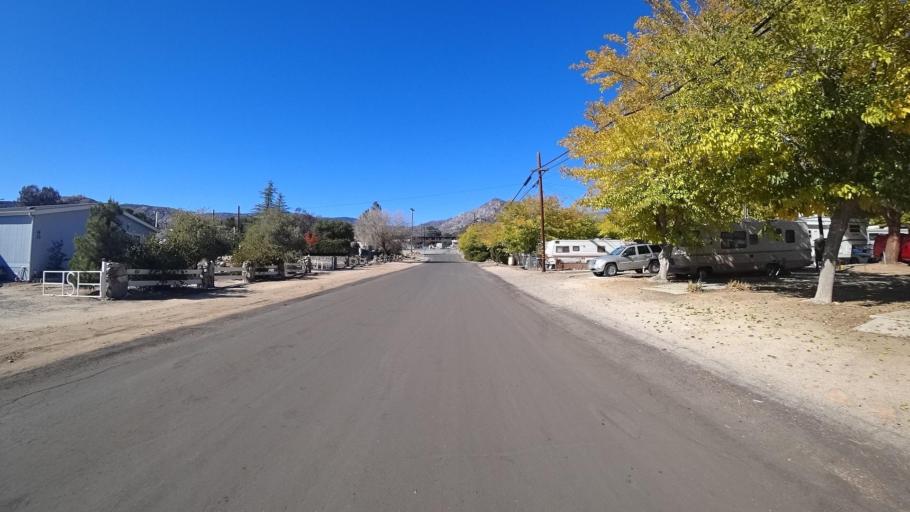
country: US
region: California
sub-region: Kern County
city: Wofford Heights
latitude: 35.7066
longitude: -118.4548
